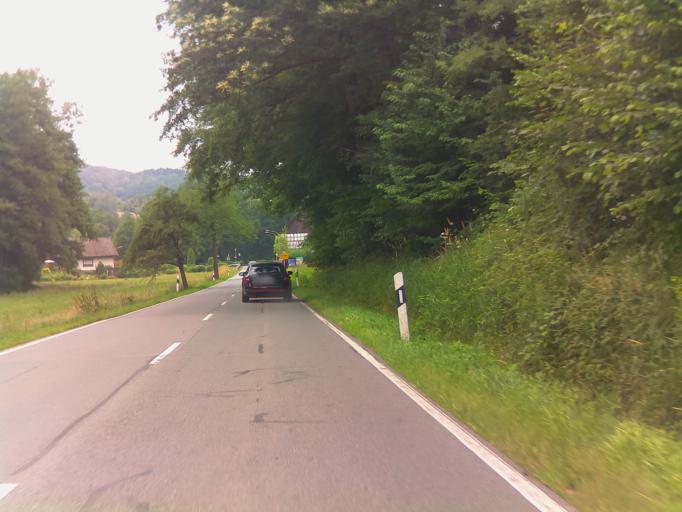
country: DE
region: Hesse
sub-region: Regierungsbezirk Darmstadt
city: Lindenfels
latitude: 49.6738
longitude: 8.7667
